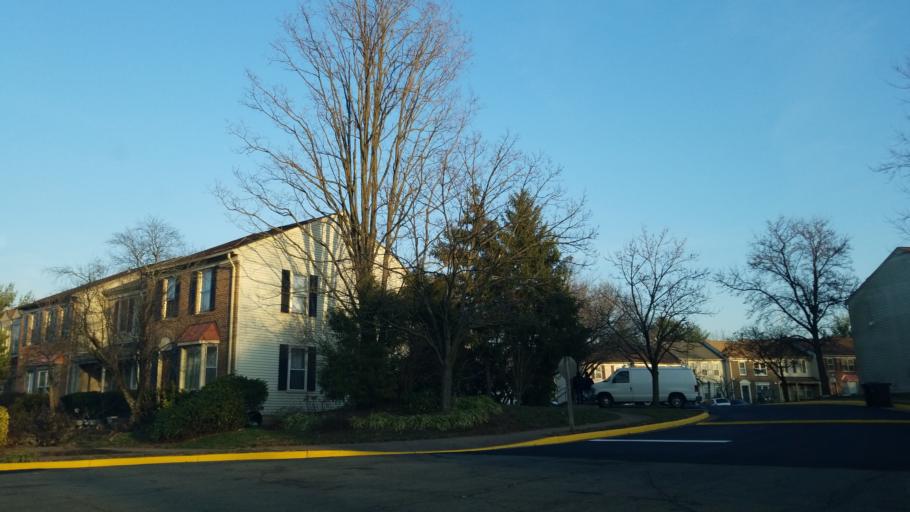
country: US
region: Virginia
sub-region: Fairfax County
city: Centreville
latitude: 38.8462
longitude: -77.4387
